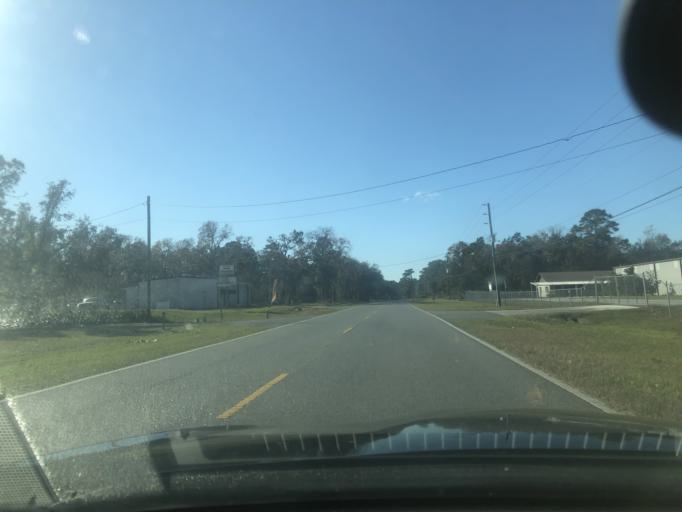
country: US
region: Florida
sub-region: Citrus County
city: Homosassa Springs
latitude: 28.8184
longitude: -82.5534
